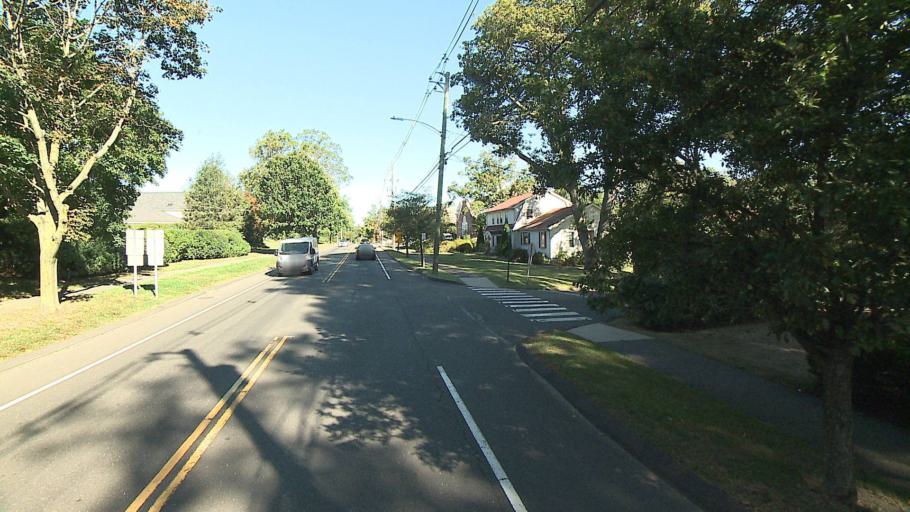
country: US
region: Connecticut
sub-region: Fairfield County
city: New Canaan
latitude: 41.1400
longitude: -73.4909
